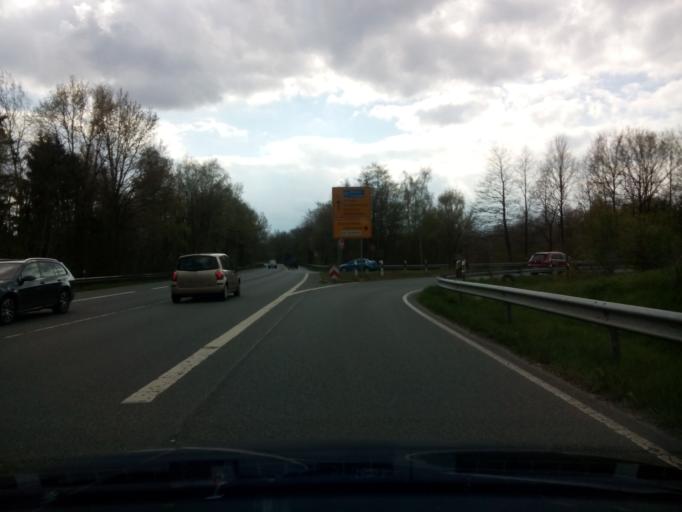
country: DE
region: Lower Saxony
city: Osterholz-Scharmbeck
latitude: 53.2376
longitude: 8.7815
